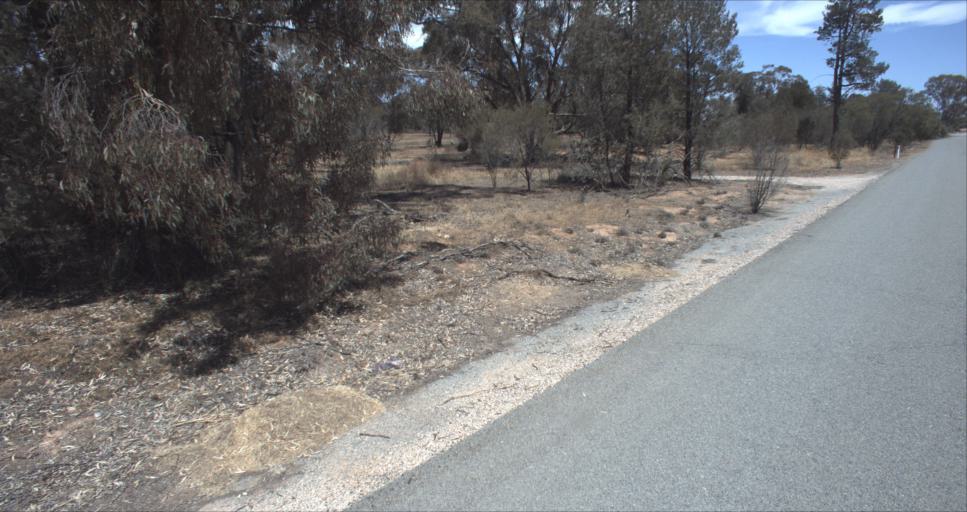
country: AU
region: New South Wales
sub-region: Leeton
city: Leeton
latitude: -34.6726
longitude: 146.4372
